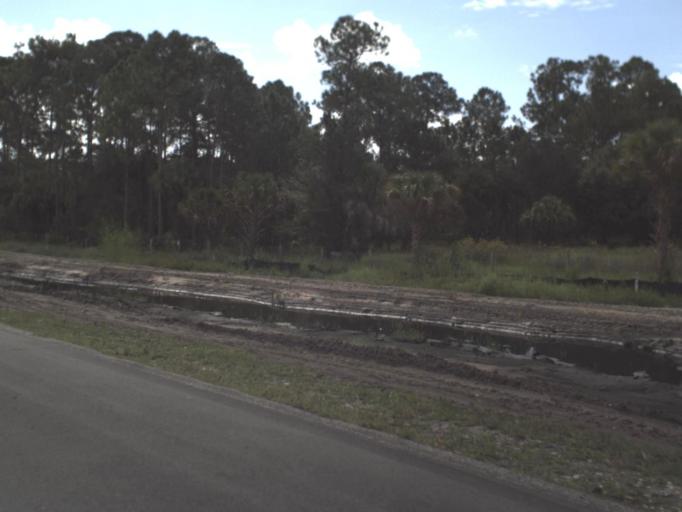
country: US
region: Florida
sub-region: Sarasota County
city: Warm Mineral Springs
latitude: 27.0997
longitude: -82.2564
